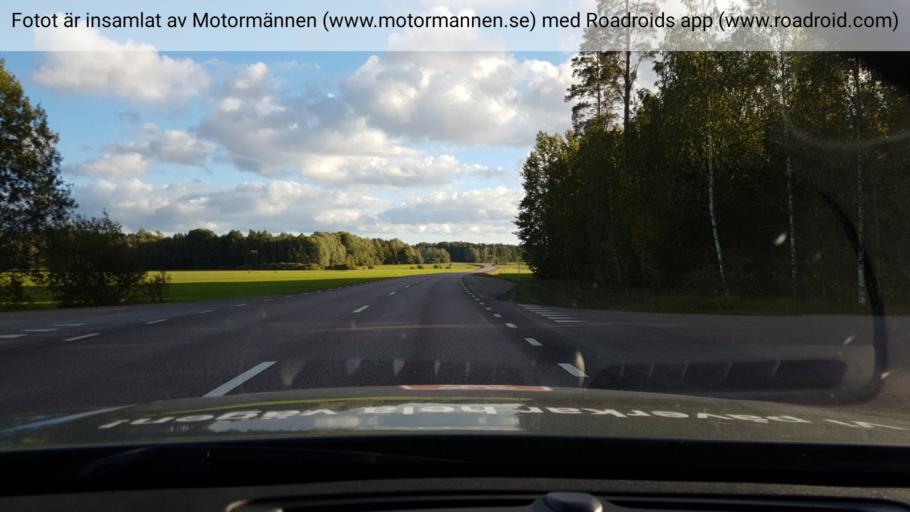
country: SE
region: Vaermland
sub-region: Karlstads Kommun
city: Molkom
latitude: 59.6234
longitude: 13.7305
